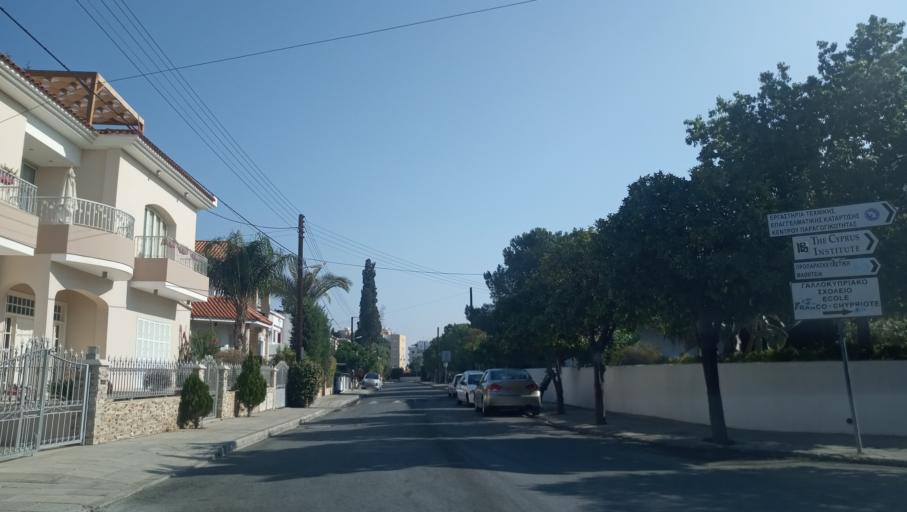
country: CY
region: Lefkosia
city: Nicosia
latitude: 35.1428
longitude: 33.3788
